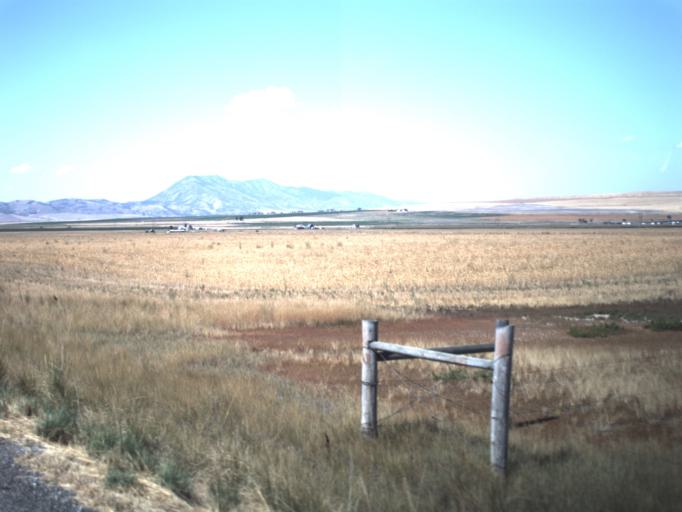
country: US
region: Utah
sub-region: Cache County
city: Benson
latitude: 41.8450
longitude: -111.9354
